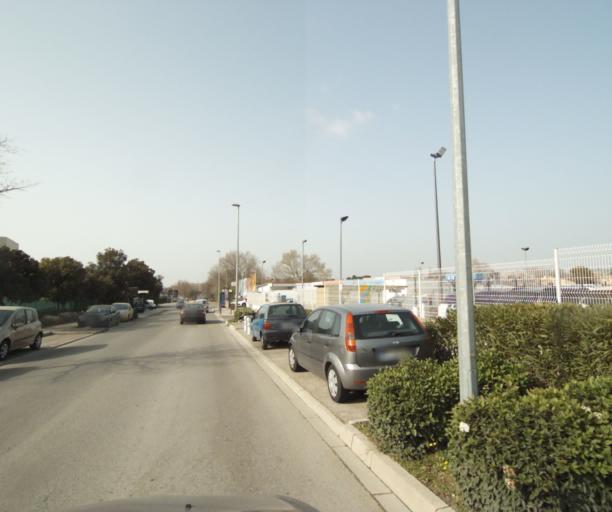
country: FR
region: Provence-Alpes-Cote d'Azur
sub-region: Departement des Bouches-du-Rhone
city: Les Pennes-Mirabeau
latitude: 43.4174
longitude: 5.2937
